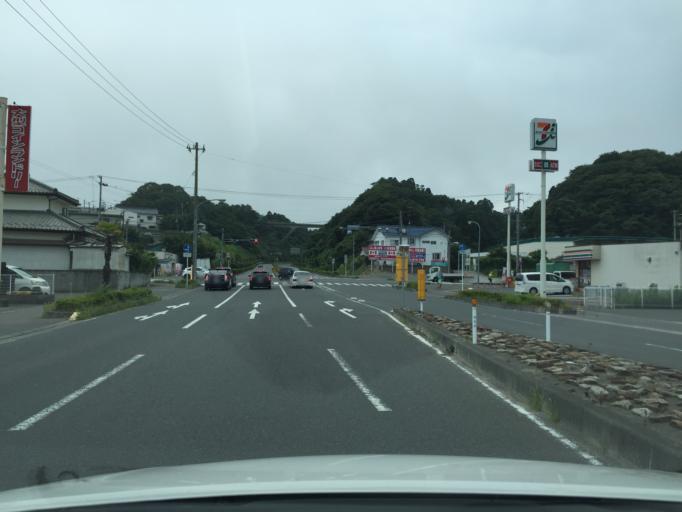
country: JP
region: Fukushima
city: Iwaki
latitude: 36.9503
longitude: 140.9210
